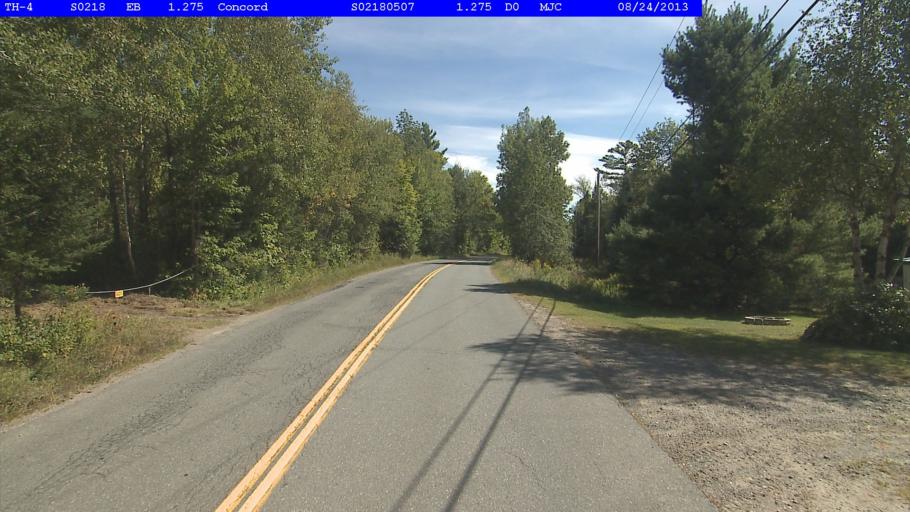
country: US
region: New Hampshire
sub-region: Grafton County
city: Littleton
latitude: 44.4479
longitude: -71.7663
